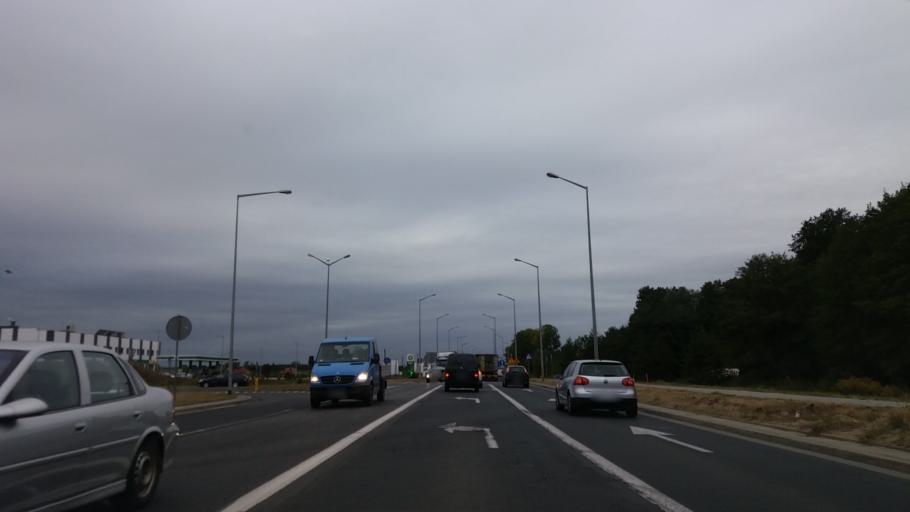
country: PL
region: Lubusz
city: Gorzow Wielkopolski
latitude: 52.6992
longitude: 15.2321
